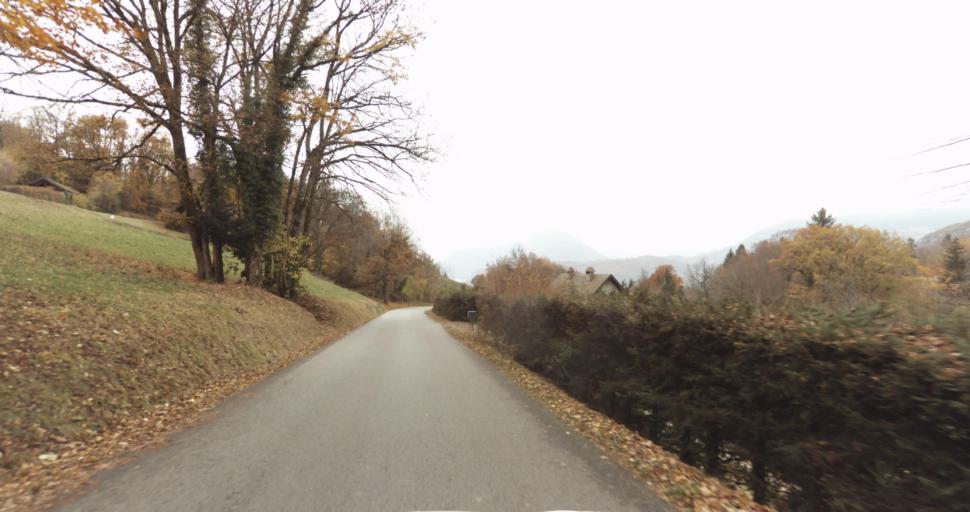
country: FR
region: Rhone-Alpes
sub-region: Departement de la Haute-Savoie
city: Talloires
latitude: 45.8177
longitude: 6.1969
